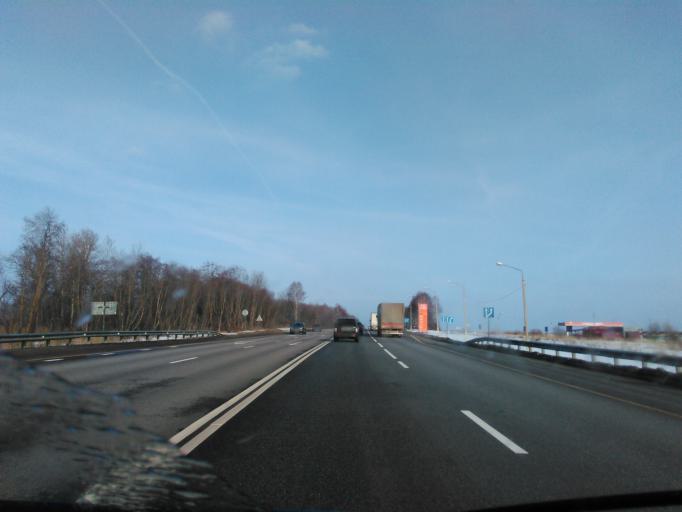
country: RU
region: Smolensk
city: Vyaz'ma
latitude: 55.2107
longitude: 34.1607
